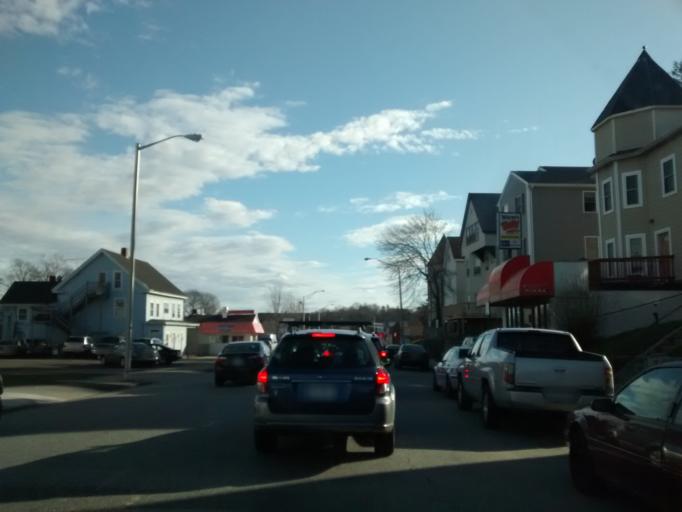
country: US
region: Massachusetts
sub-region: Worcester County
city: Worcester
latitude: 42.2923
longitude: -71.8051
